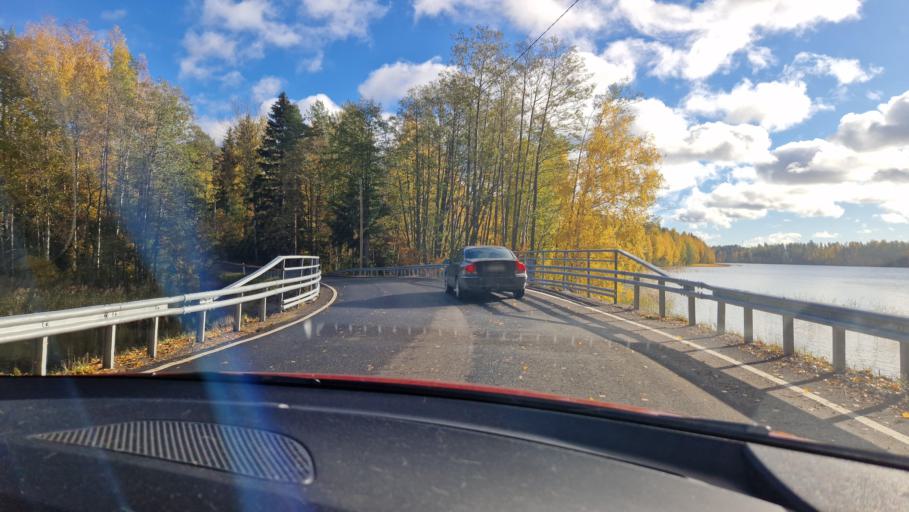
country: FI
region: South Karelia
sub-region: Lappeenranta
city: Lemi
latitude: 60.9650
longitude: 27.7533
